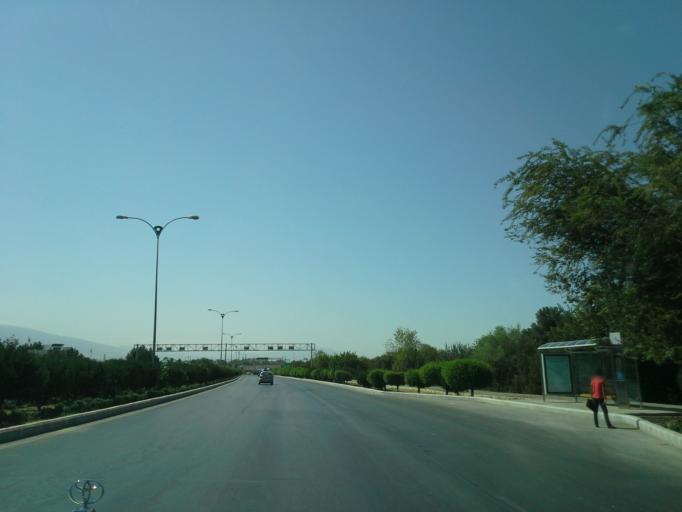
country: TM
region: Ahal
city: Annau
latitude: 37.9116
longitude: 58.4951
